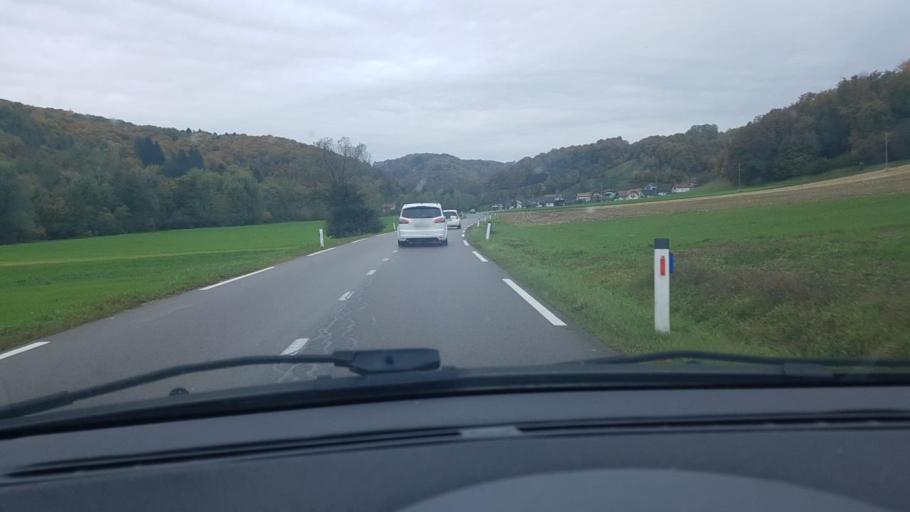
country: SI
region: Majsperk
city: Majsperk
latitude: 46.3326
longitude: 15.7326
